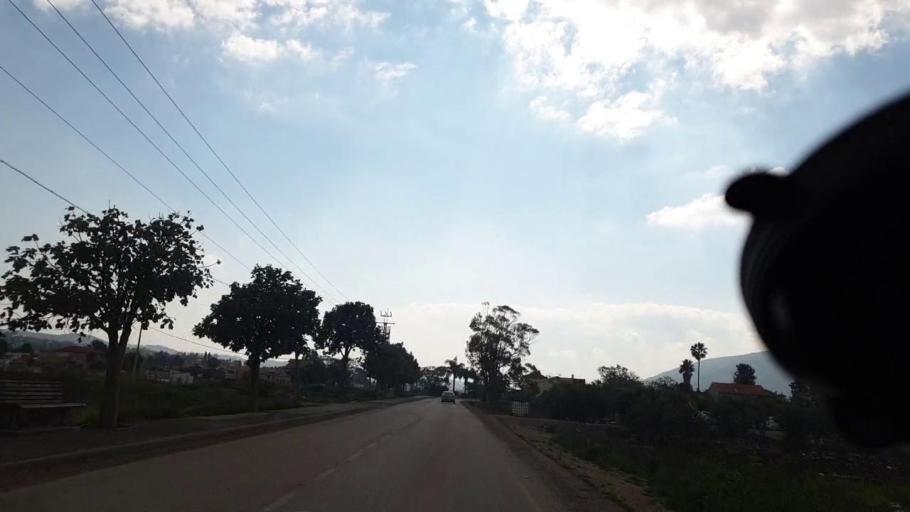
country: IL
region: Haifa
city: Rekhasim
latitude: 32.7519
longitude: 35.0871
